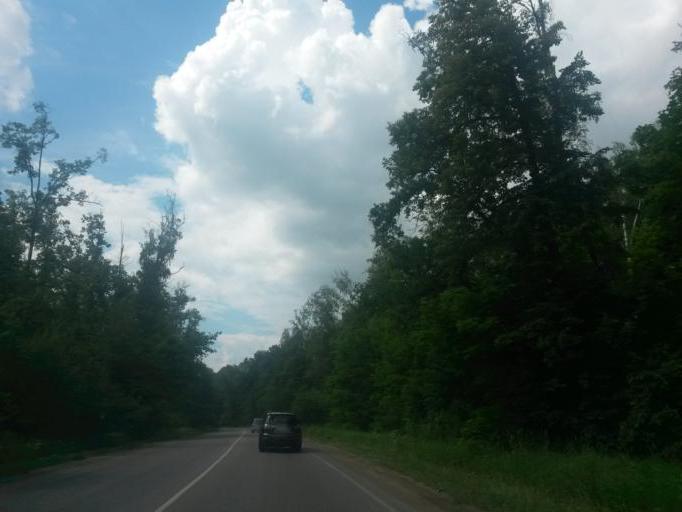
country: RU
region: Moskovskaya
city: Gorki-Leninskiye
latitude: 55.5120
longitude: 37.8052
